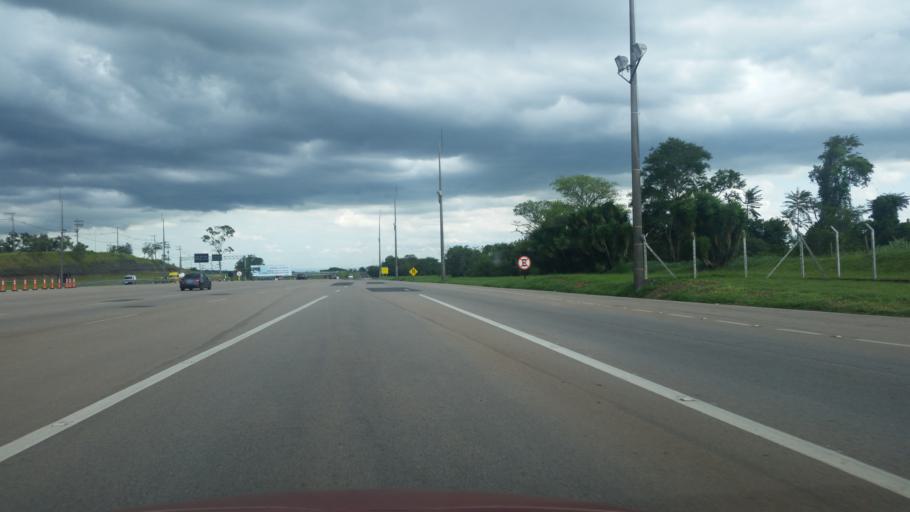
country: BR
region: Sao Paulo
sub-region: Boituva
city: Boituva
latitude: -23.3142
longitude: -47.6434
